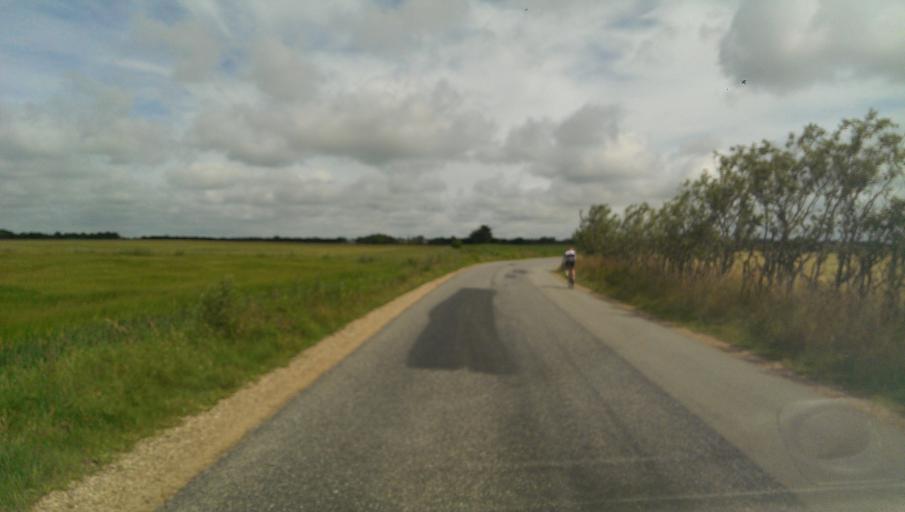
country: DK
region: South Denmark
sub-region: Esbjerg Kommune
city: Tjaereborg
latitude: 55.5057
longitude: 8.5744
